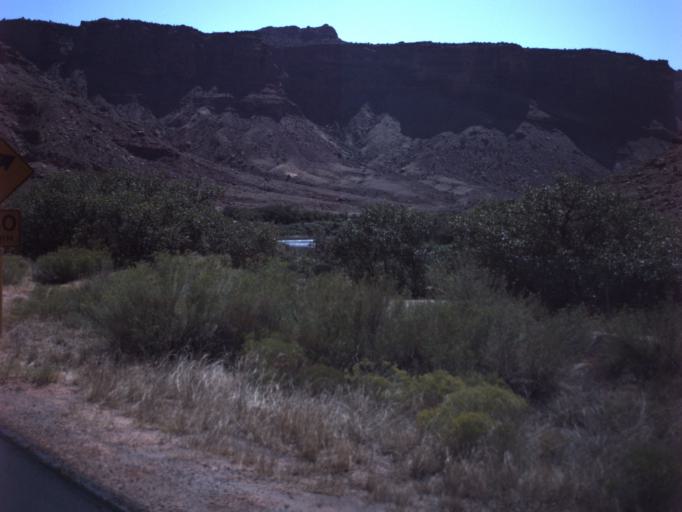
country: US
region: Utah
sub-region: Grand County
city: Moab
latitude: 38.6482
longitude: -109.4784
